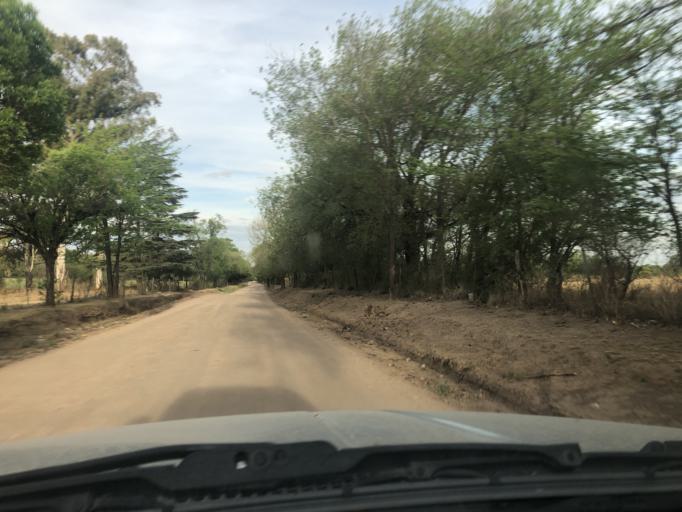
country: AR
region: Cordoba
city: La Granja
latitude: -31.0176
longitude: -64.2470
